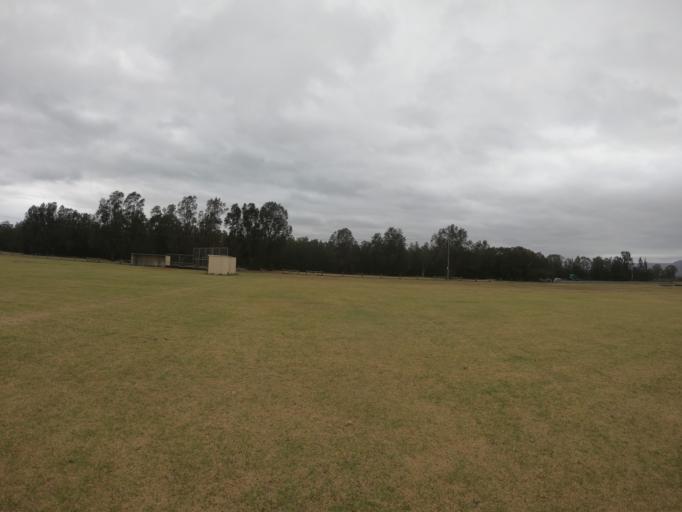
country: AU
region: New South Wales
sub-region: Wollongong
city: Berkeley
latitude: -34.4834
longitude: 150.8345
